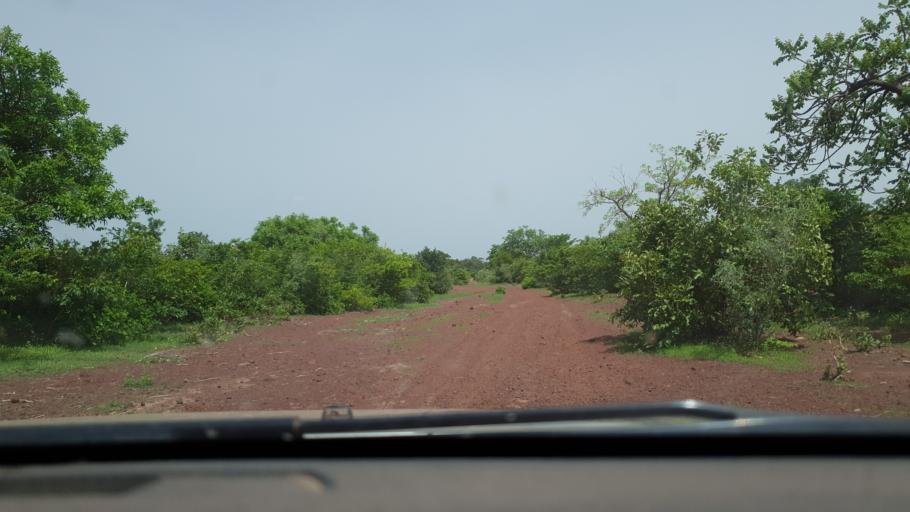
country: ML
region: Koulikoro
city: Koulikoro
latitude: 12.6666
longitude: -7.2358
